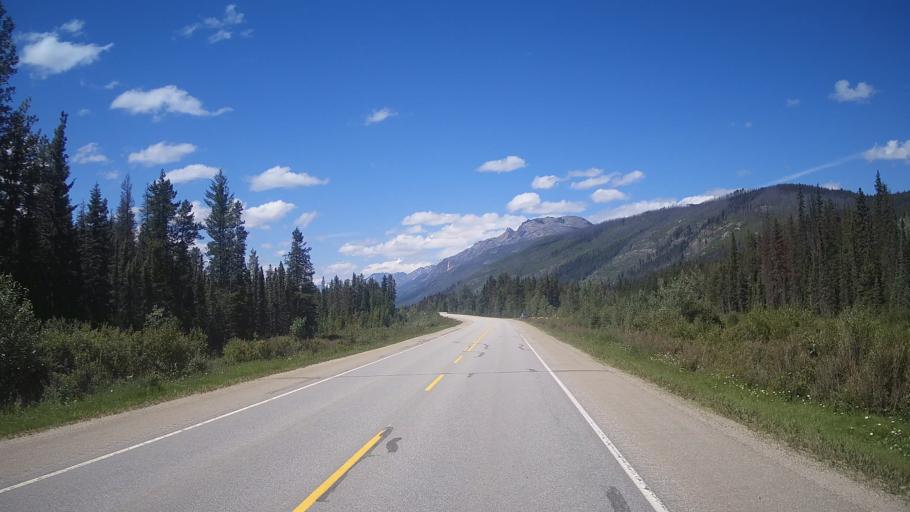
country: CA
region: Alberta
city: Jasper Park Lodge
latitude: 52.9165
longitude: -118.7947
